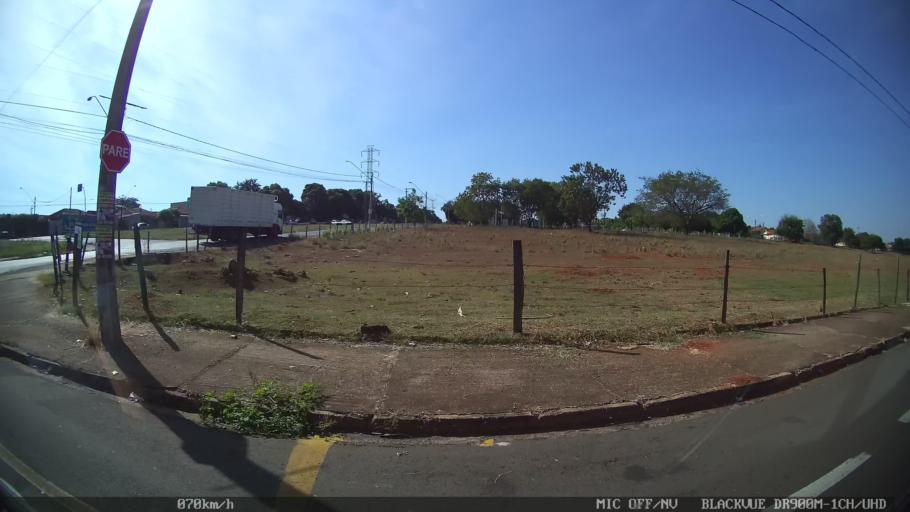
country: BR
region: Sao Paulo
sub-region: Sao Jose Do Rio Preto
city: Sao Jose do Rio Preto
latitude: -20.7897
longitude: -49.4113
